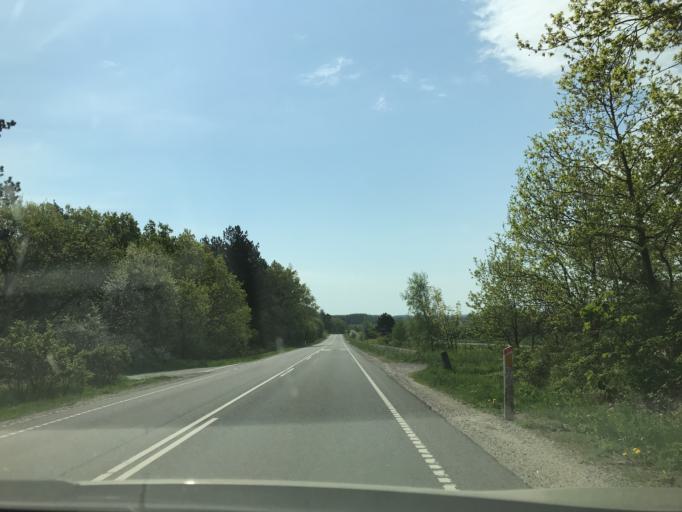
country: DK
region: South Denmark
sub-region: Middelfart Kommune
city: Ejby
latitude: 55.3904
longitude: 9.9139
